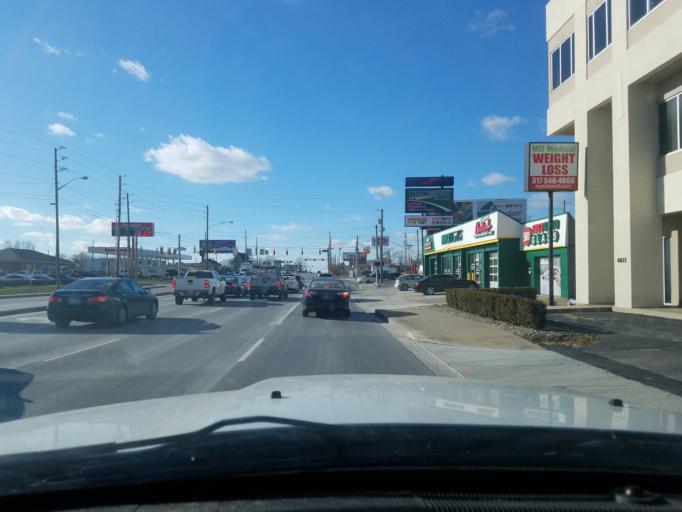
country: US
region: Indiana
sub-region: Hamilton County
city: Fishers
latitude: 39.9053
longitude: -86.0486
